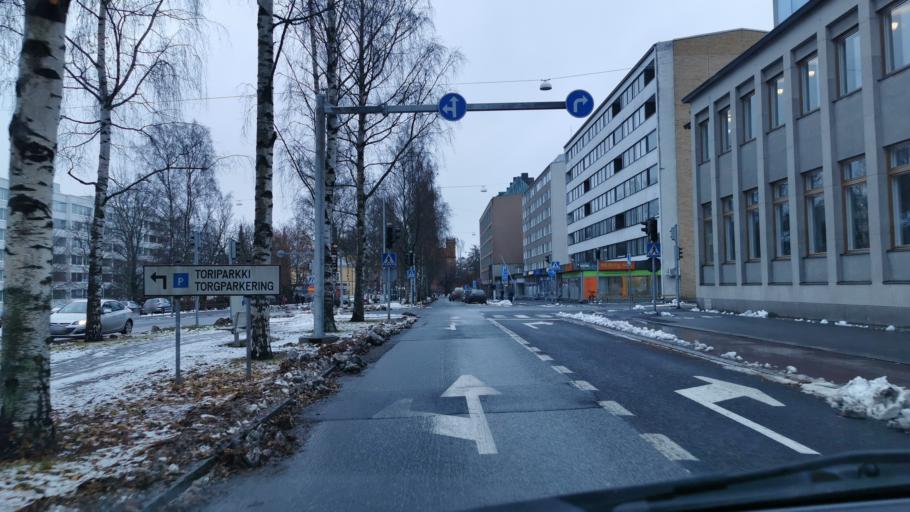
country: FI
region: Ostrobothnia
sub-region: Vaasa
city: Vaasa
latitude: 63.0973
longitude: 21.6077
